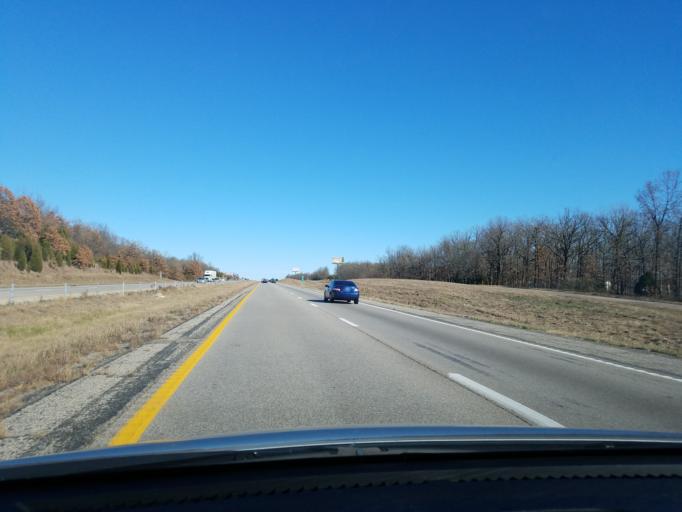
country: US
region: Missouri
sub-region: Laclede County
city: Lebanon
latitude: 37.5850
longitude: -92.7419
